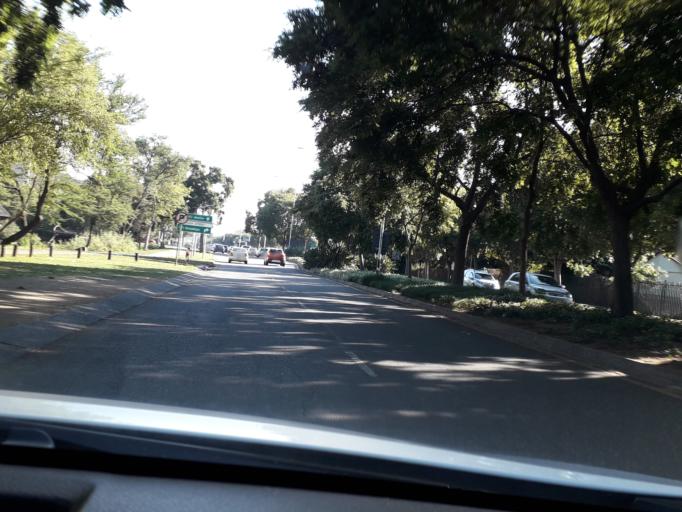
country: ZA
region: Gauteng
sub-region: City of Tshwane Metropolitan Municipality
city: Pretoria
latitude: -25.7561
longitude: 28.1965
